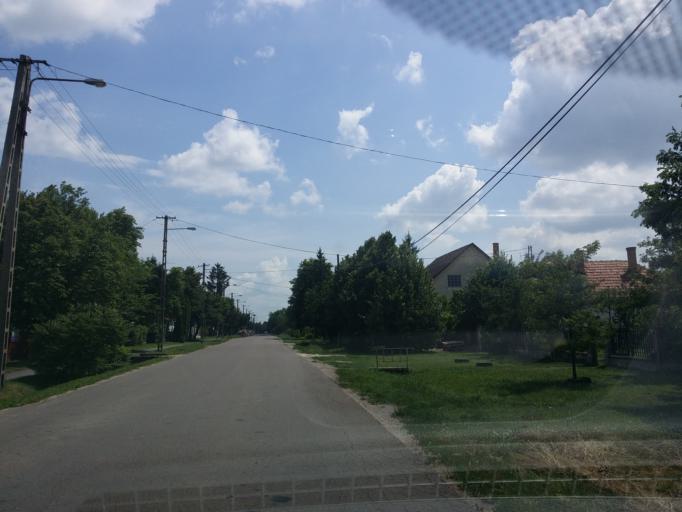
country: HU
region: Heves
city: Tiszanana
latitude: 47.5980
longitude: 20.5872
